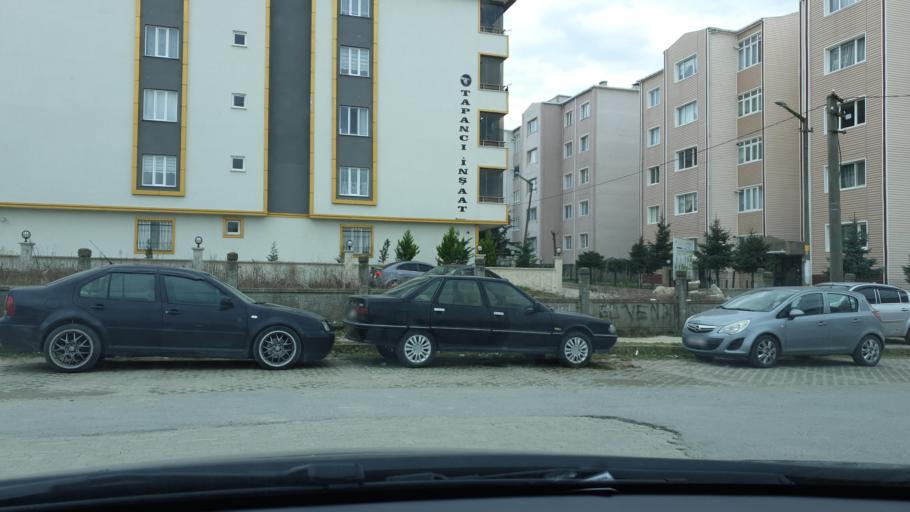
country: TR
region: Tekirdag
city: Cerkezkoey
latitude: 41.2851
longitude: 27.9820
